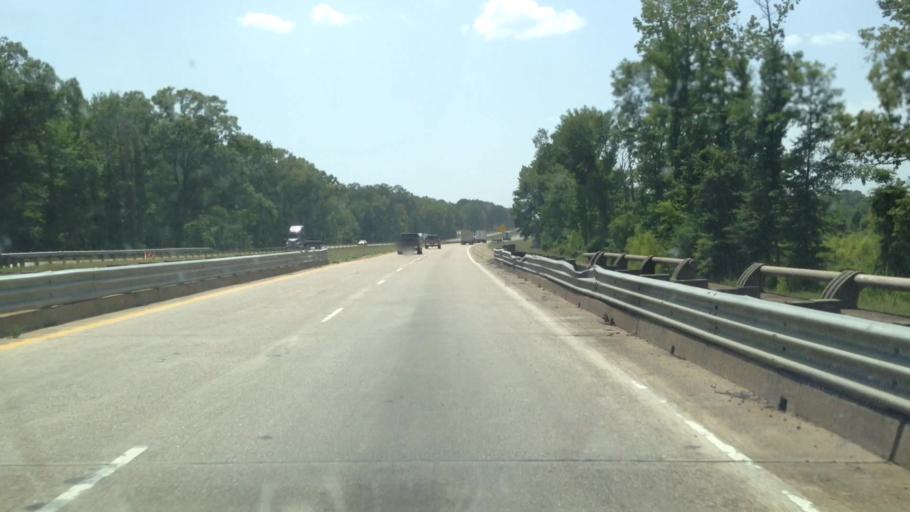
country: US
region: Louisiana
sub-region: Webster Parish
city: Minden
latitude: 32.5619
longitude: -93.1486
